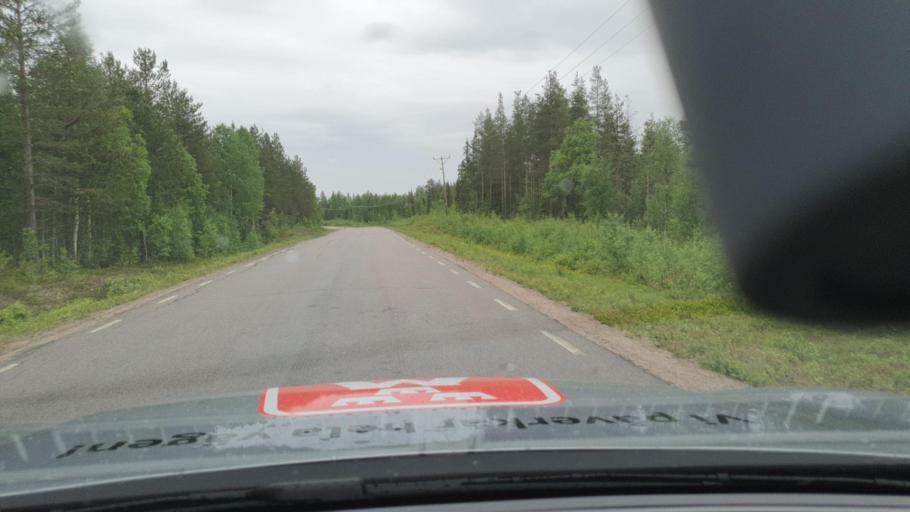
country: SE
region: Norrbotten
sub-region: Pajala Kommun
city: Pajala
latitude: 66.7540
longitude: 23.1593
